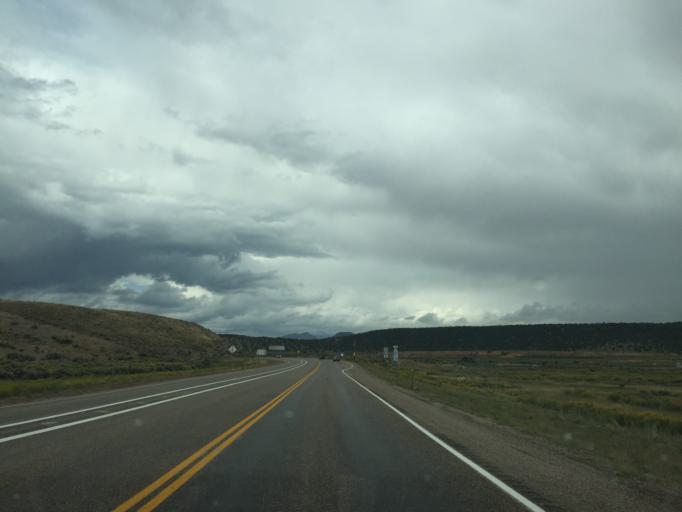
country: US
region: Utah
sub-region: Garfield County
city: Panguitch
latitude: 37.7467
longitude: -112.3784
